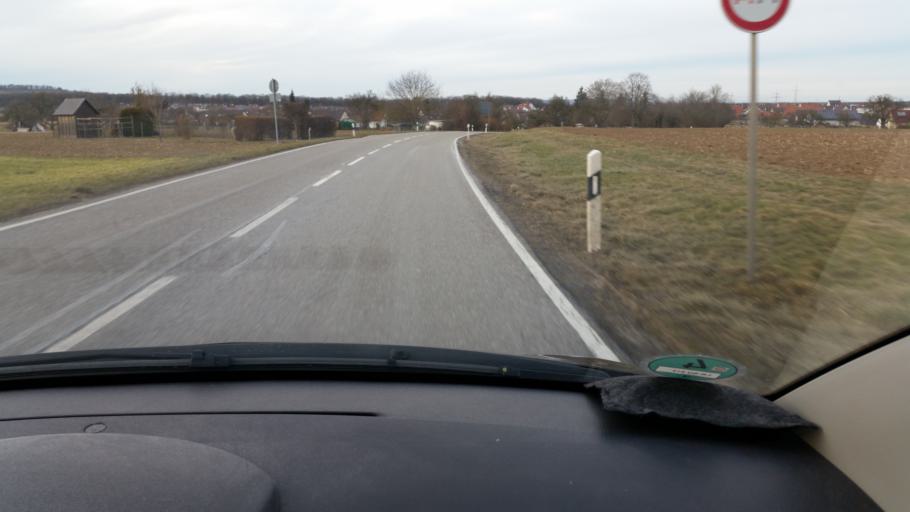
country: DE
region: Baden-Wuerttemberg
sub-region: Regierungsbezirk Stuttgart
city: Lochgau
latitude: 48.9963
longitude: 9.1041
